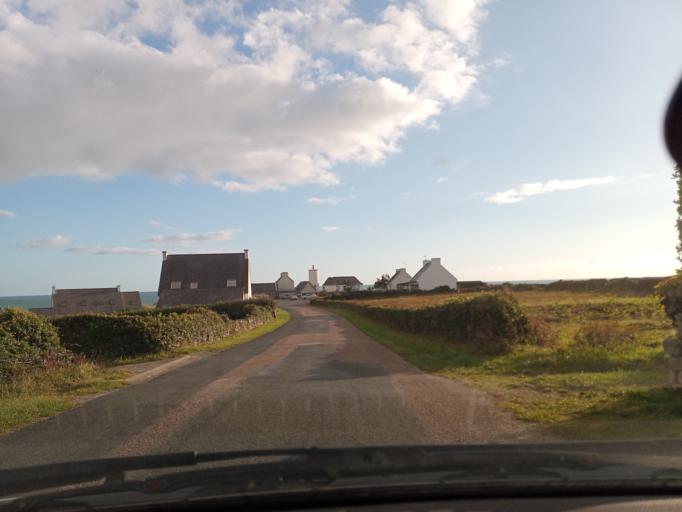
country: FR
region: Brittany
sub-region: Departement du Finistere
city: Esquibien
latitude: 48.0027
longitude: -4.5653
